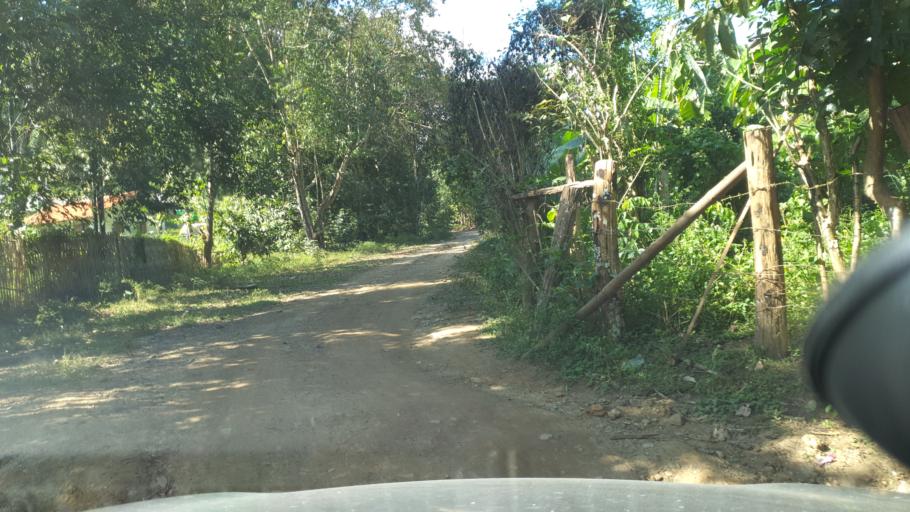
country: TH
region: Mae Hong Son
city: Mae Hi
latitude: 19.2965
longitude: 98.7057
